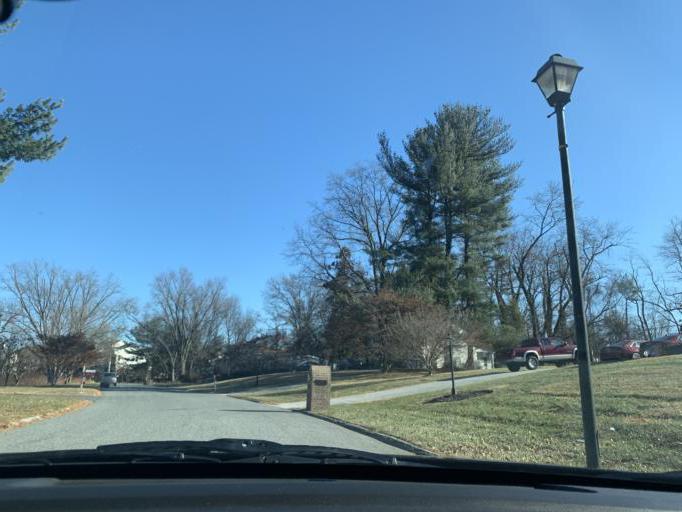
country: US
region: Maryland
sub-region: Baltimore County
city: Garrison
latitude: 39.3934
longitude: -76.7525
